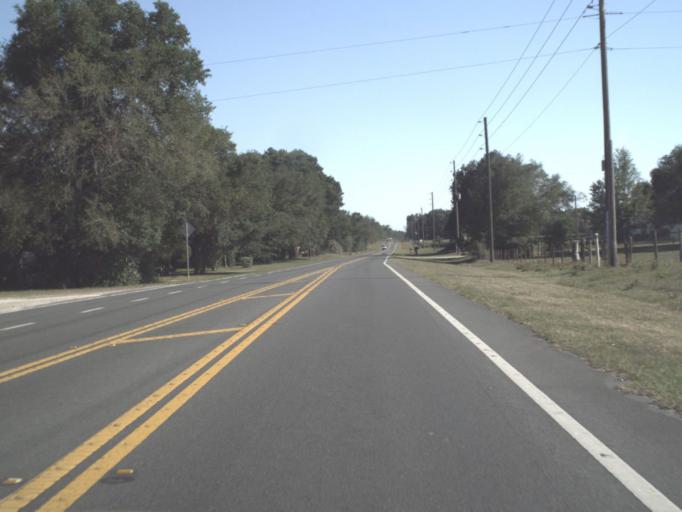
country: US
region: Florida
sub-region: Marion County
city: Dunnellon
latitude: 29.1601
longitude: -82.4405
